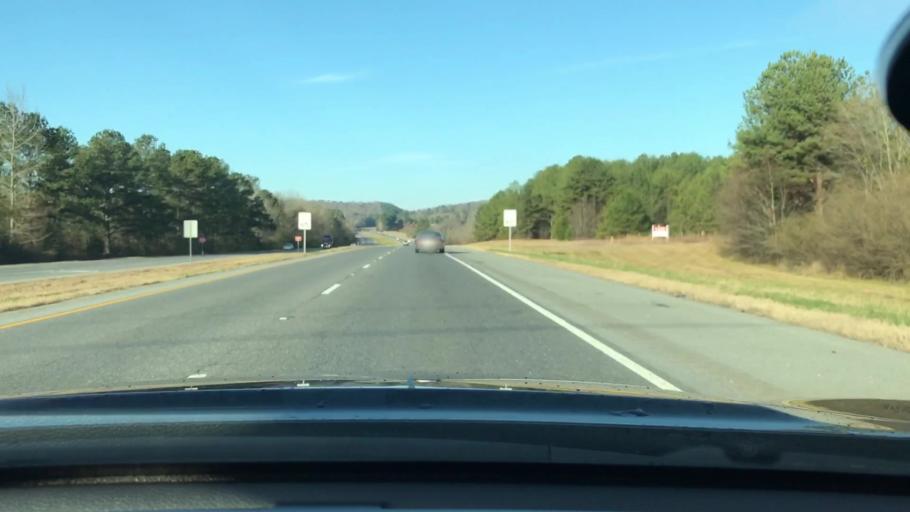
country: US
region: Alabama
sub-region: Shelby County
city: Harpersville
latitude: 33.3494
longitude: -86.4614
